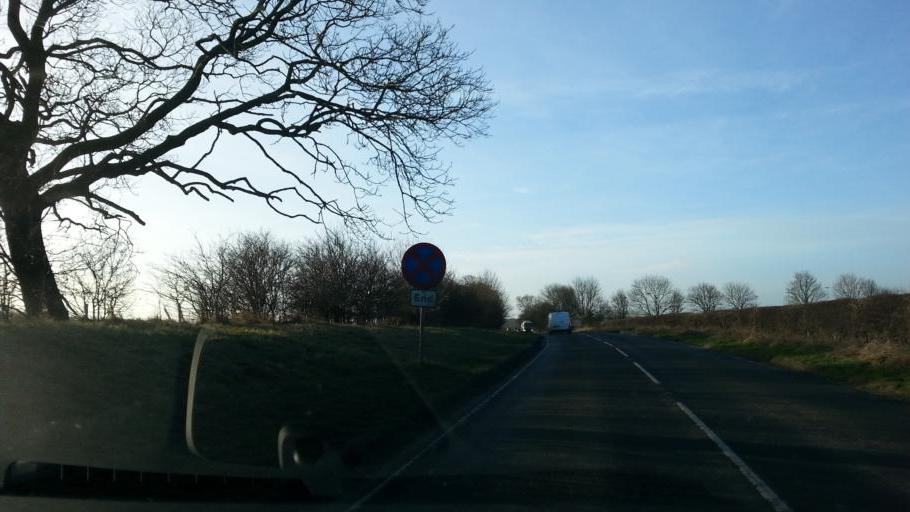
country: GB
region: England
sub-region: Lincolnshire
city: Grantham
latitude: 52.8943
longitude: -0.5932
